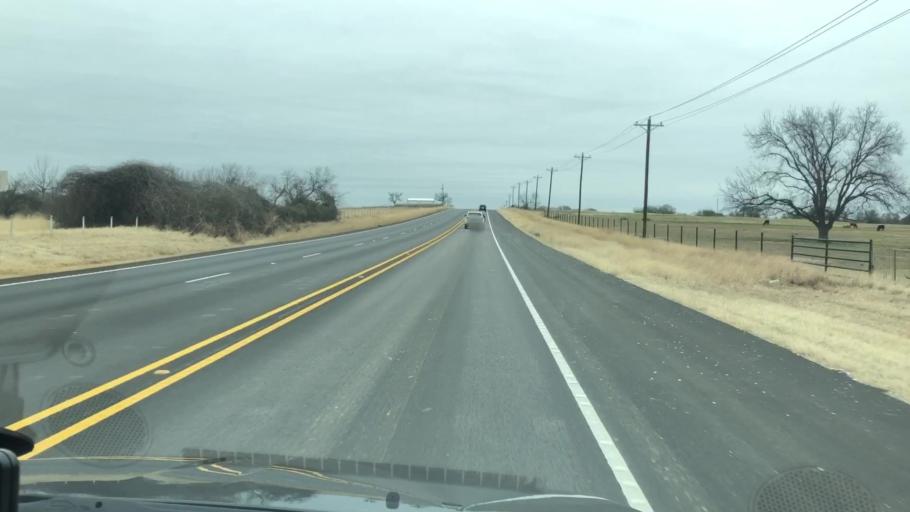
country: US
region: Texas
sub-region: Erath County
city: Stephenville
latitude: 32.2914
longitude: -98.1905
